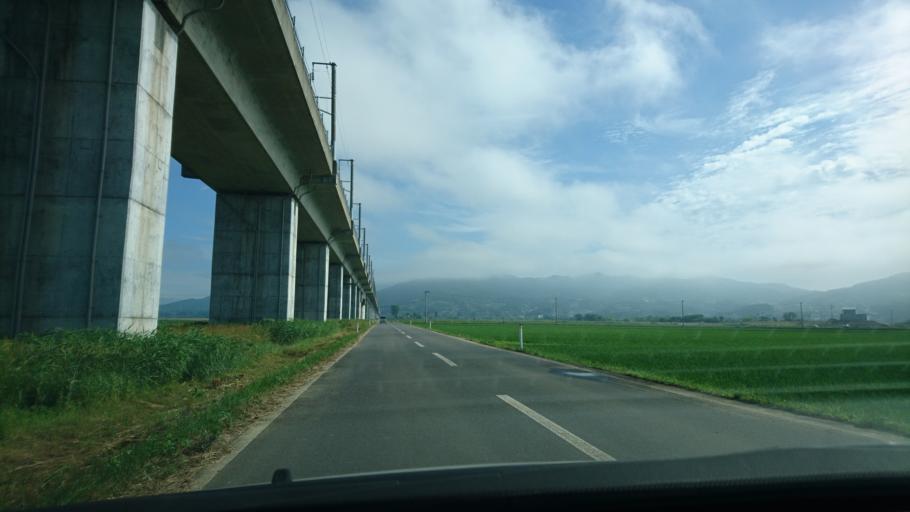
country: JP
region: Iwate
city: Ichinoseki
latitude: 38.9539
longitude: 141.1496
